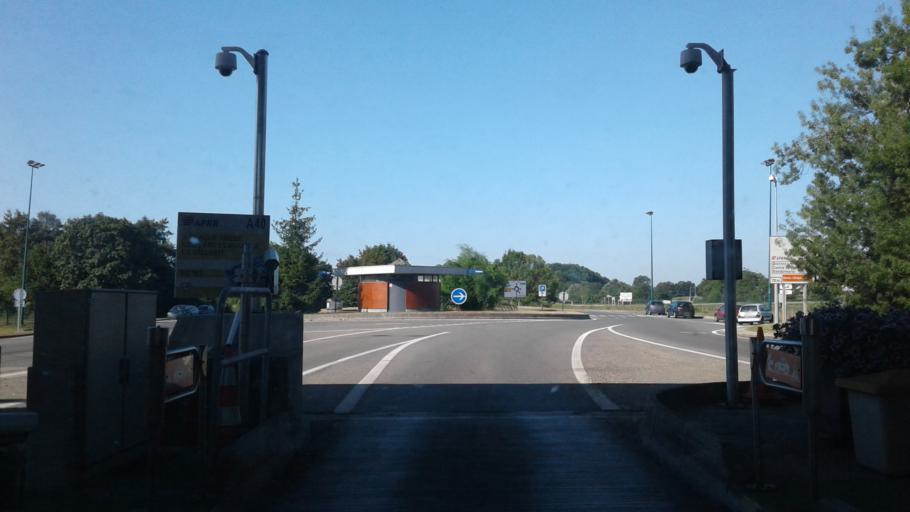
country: FR
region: Rhone-Alpes
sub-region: Departement de l'Ain
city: Certines
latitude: 46.1458
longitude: 5.2863
